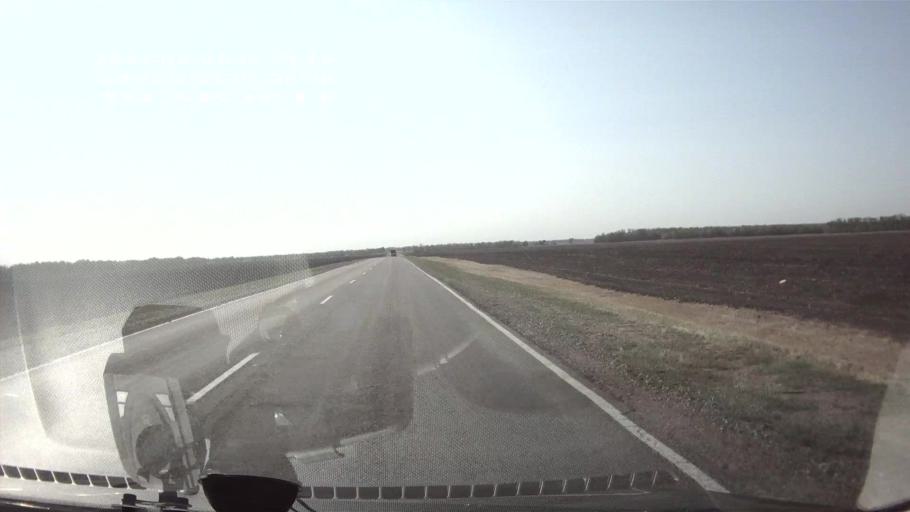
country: RU
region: Krasnodarskiy
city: Belaya Glina
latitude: 46.0303
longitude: 40.7987
